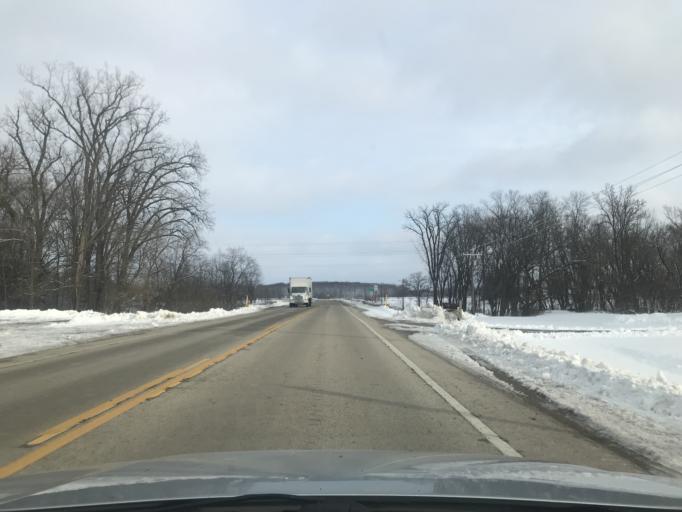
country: US
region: Wisconsin
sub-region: Oconto County
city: Oconto Falls
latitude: 44.8883
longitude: -88.0117
